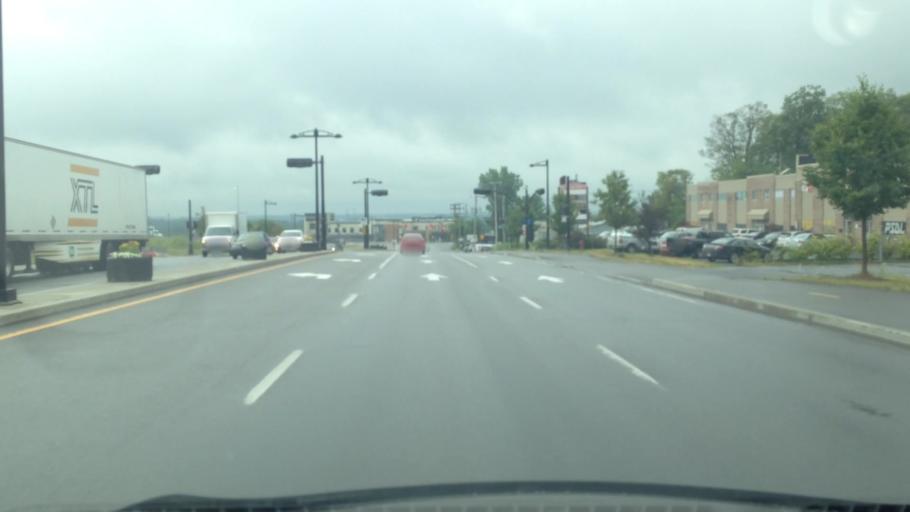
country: CA
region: Quebec
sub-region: Laurentides
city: Saint-Jerome
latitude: 45.7582
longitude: -74.0240
